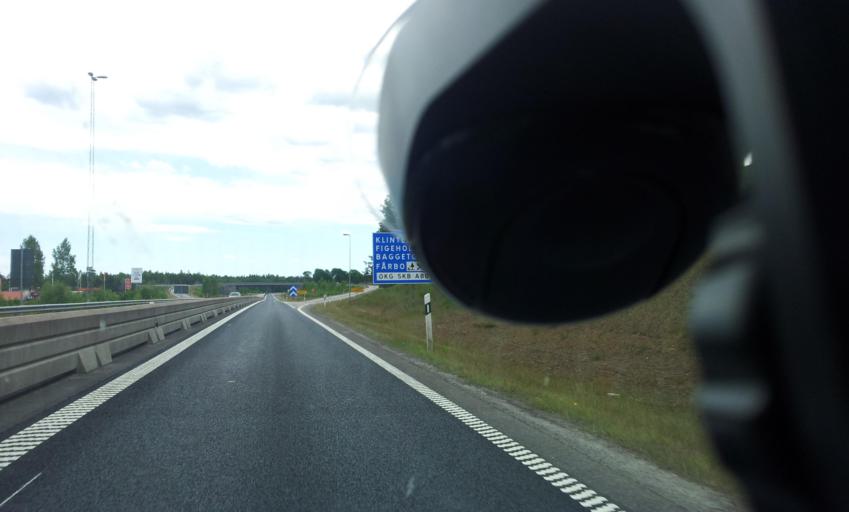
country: SE
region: Kalmar
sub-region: Oskarshamns Kommun
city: Oskarshamn
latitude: 57.3768
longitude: 16.4859
